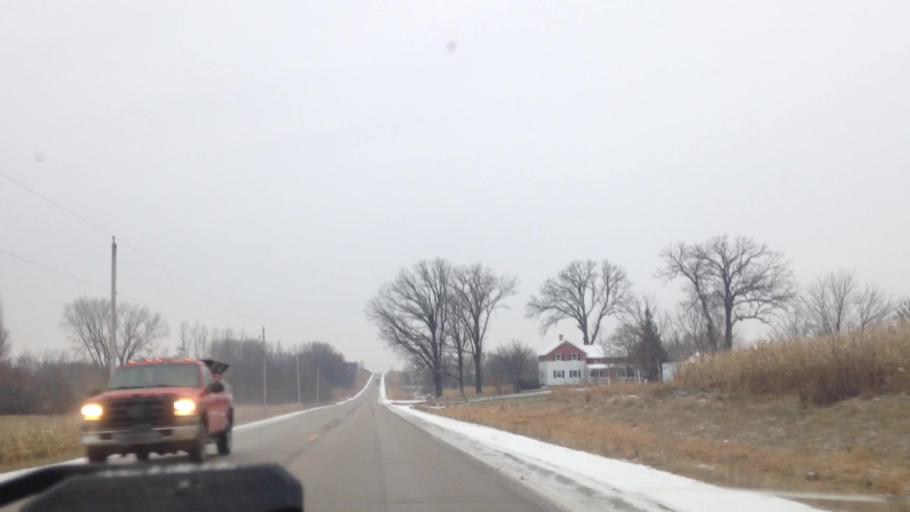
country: US
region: Wisconsin
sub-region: Dodge County
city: Hustisford
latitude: 43.3944
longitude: -88.5417
